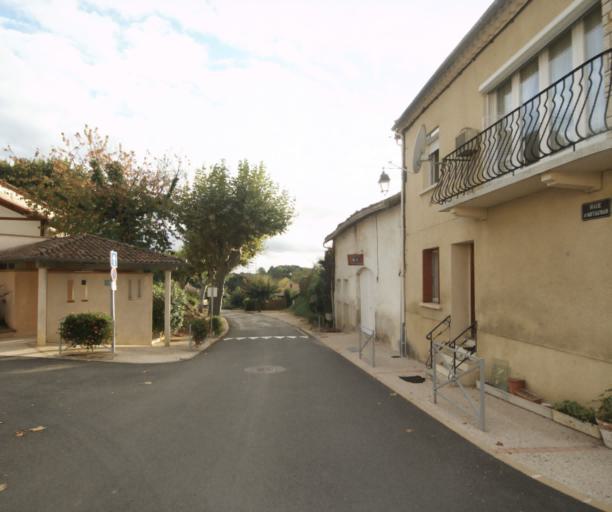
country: FR
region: Aquitaine
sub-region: Departement des Landes
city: Gabarret
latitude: 43.9483
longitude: 0.0857
